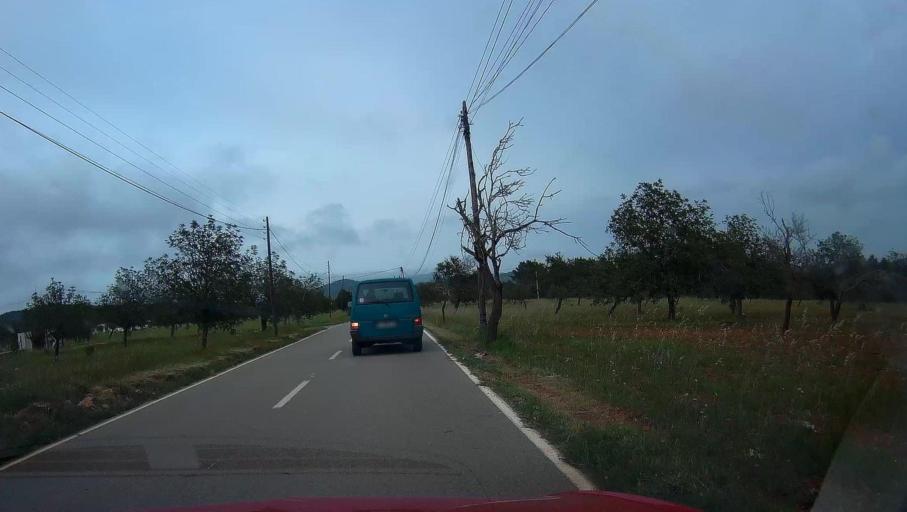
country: ES
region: Balearic Islands
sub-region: Illes Balears
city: Sant Joan de Labritja
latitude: 39.0462
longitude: 1.4135
